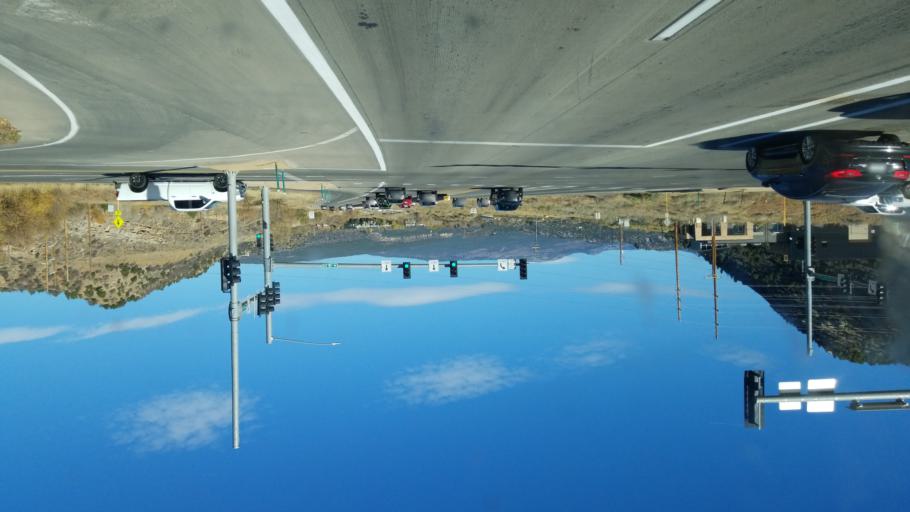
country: US
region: Colorado
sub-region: La Plata County
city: Durango
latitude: 37.2528
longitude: -107.8765
